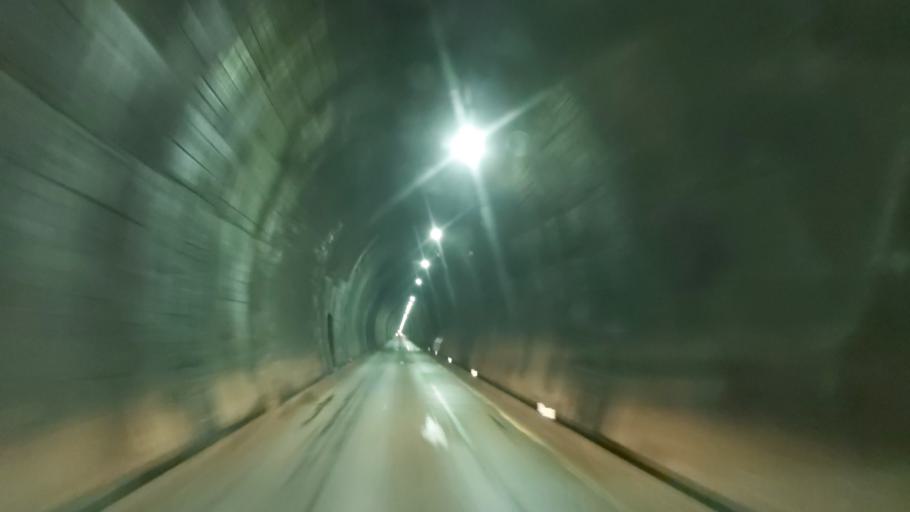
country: CL
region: Araucania
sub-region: Provincia de Cautin
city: Vilcun
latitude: -38.5469
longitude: -71.5033
